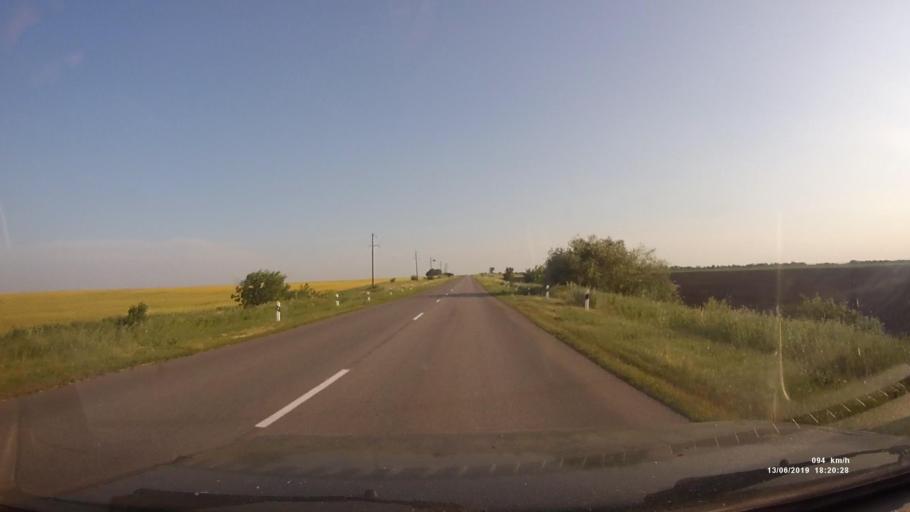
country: RU
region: Rostov
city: Kazanskaya
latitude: 49.8833
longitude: 41.2989
